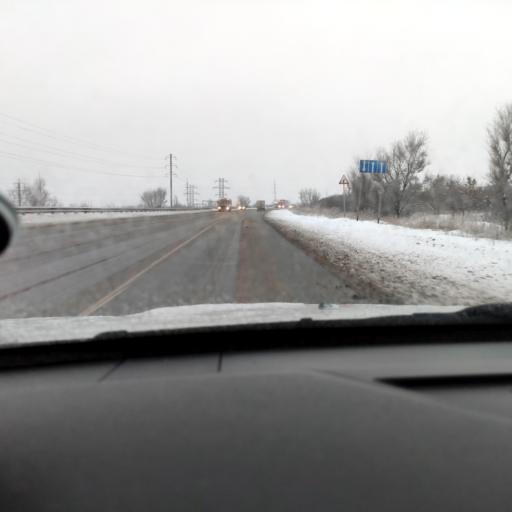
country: RU
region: Samara
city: Smyshlyayevka
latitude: 53.2431
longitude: 50.4786
